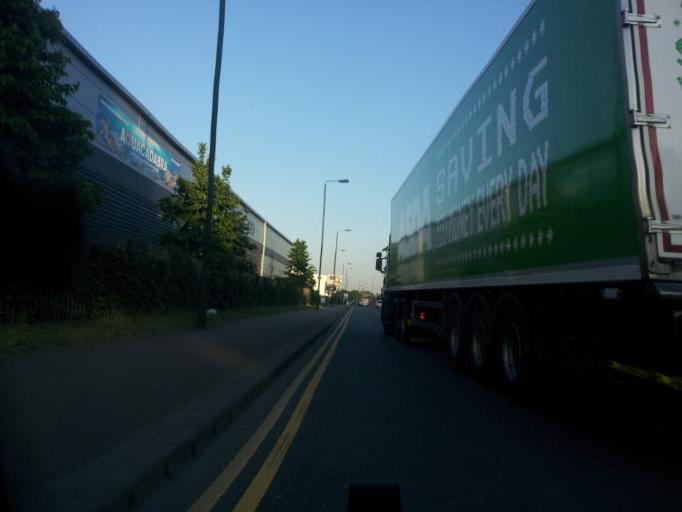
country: GB
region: England
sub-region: Greater London
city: Erith
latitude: 51.4612
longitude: 0.1902
